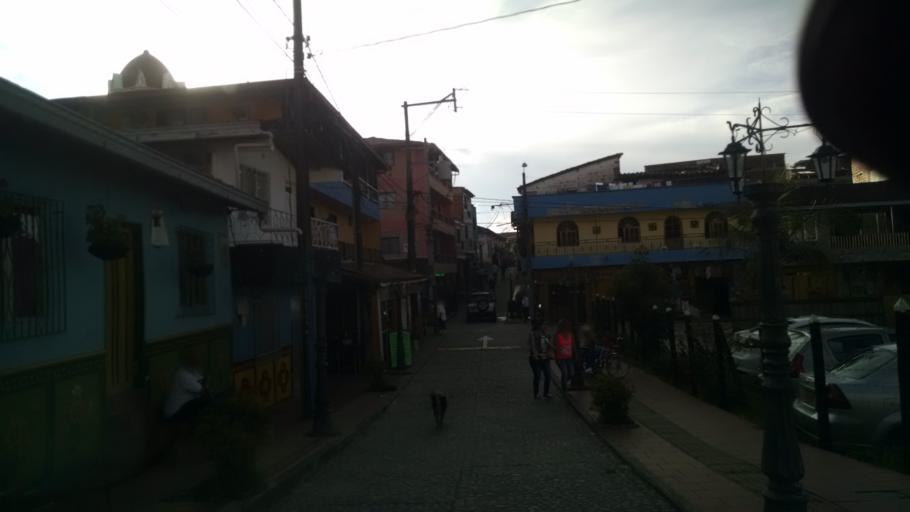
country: CO
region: Antioquia
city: Guatape
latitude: 6.2342
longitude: -75.1602
